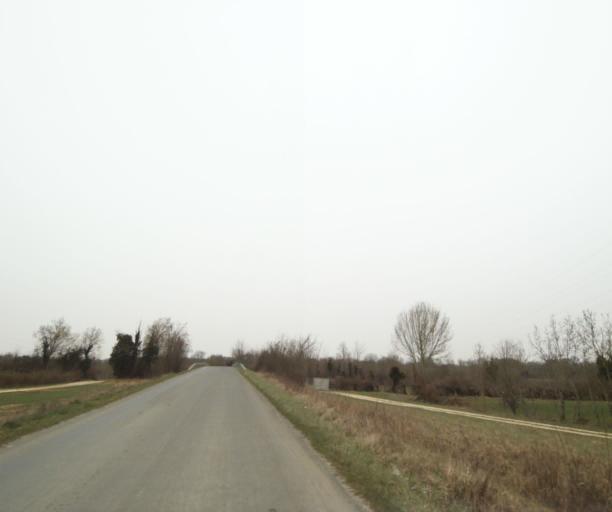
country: FR
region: Poitou-Charentes
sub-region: Departement des Deux-Sevres
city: Niort
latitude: 46.3011
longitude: -0.4783
